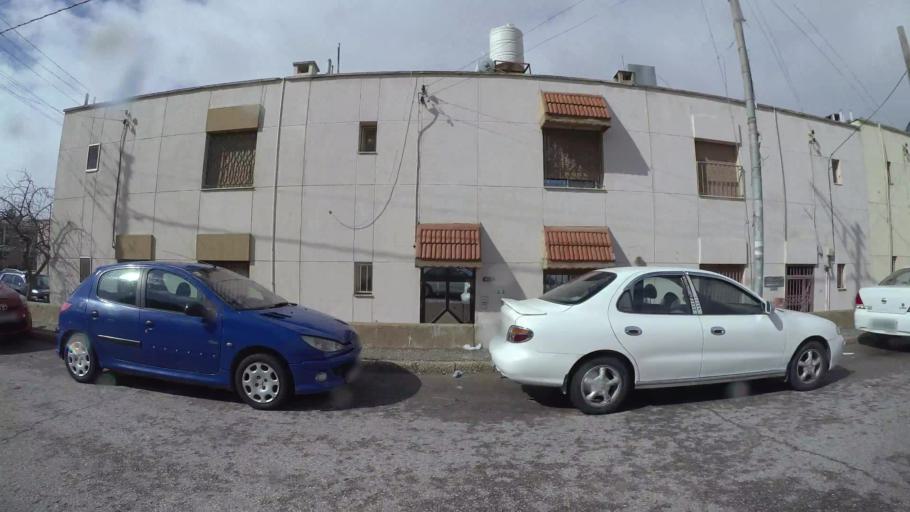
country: JO
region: Amman
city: Al Jubayhah
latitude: 32.0534
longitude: 35.8779
